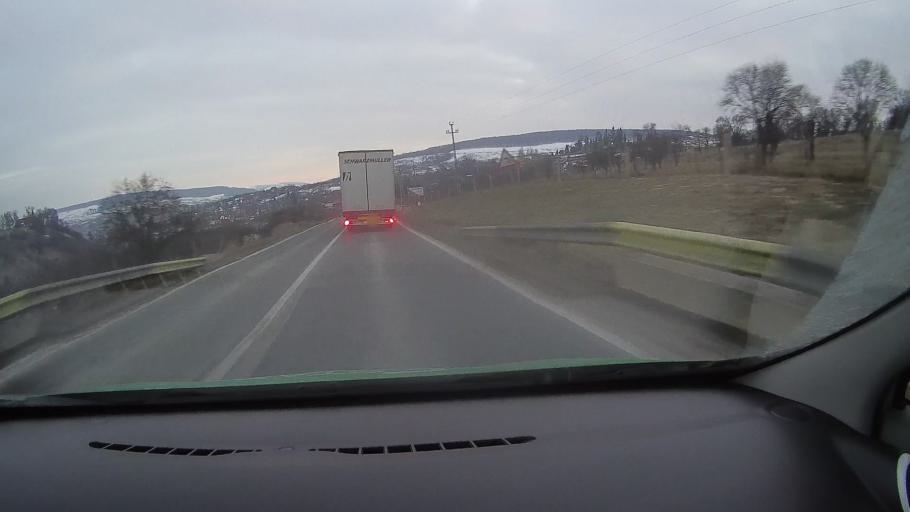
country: RO
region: Harghita
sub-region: Municipiul Odorheiu Secuiesc
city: Odorheiu Secuiesc
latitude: 46.3219
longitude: 25.2801
